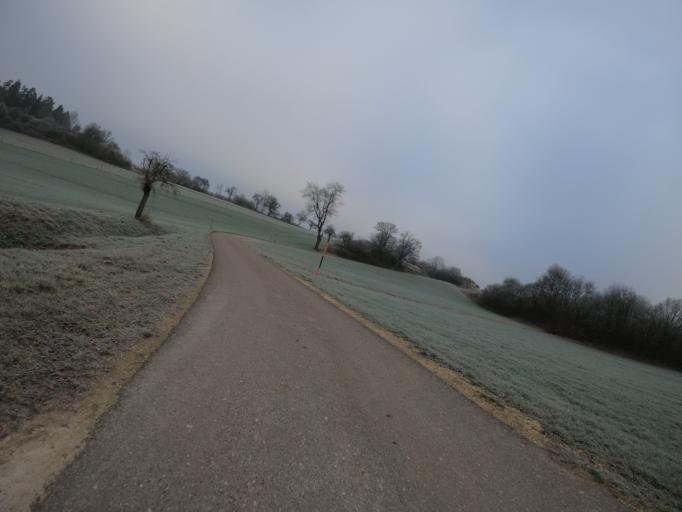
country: DE
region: Baden-Wuerttemberg
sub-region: Tuebingen Region
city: Westerstetten
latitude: 48.5137
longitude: 9.9534
